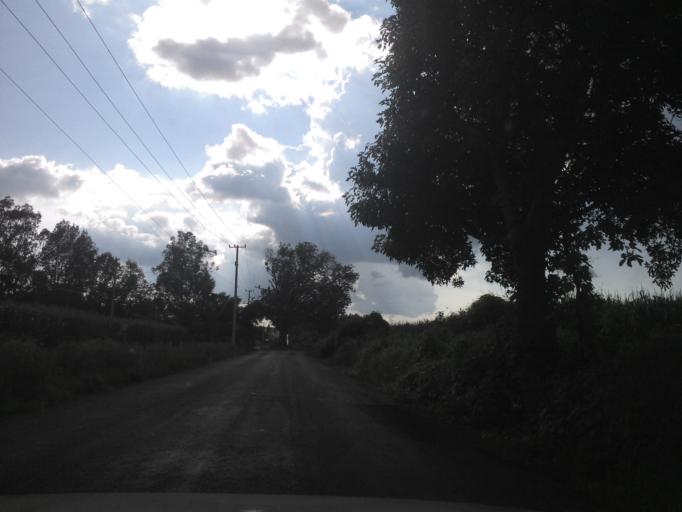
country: MX
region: Jalisco
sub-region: Atotonilco el Alto
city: Ojo de Agua de Moran
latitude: 20.6028
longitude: -102.4785
